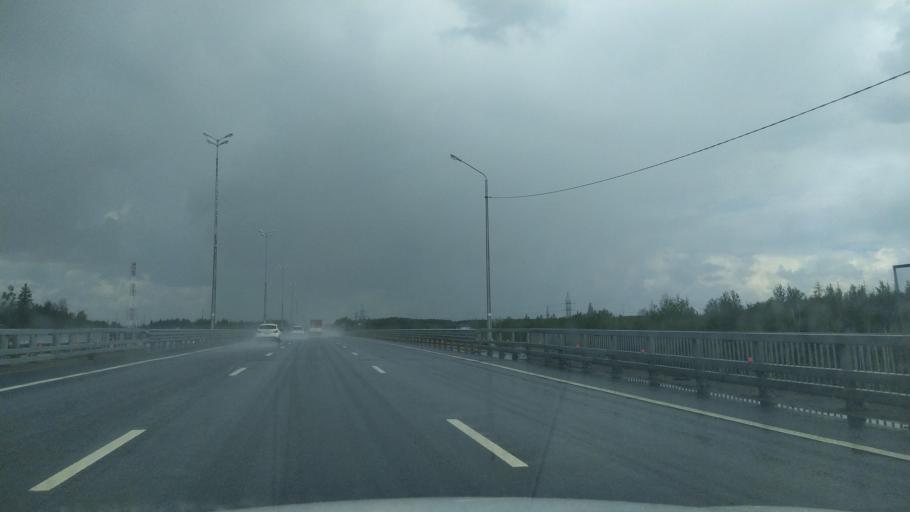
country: RU
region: Leningrad
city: Gatchina
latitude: 59.5268
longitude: 30.1233
